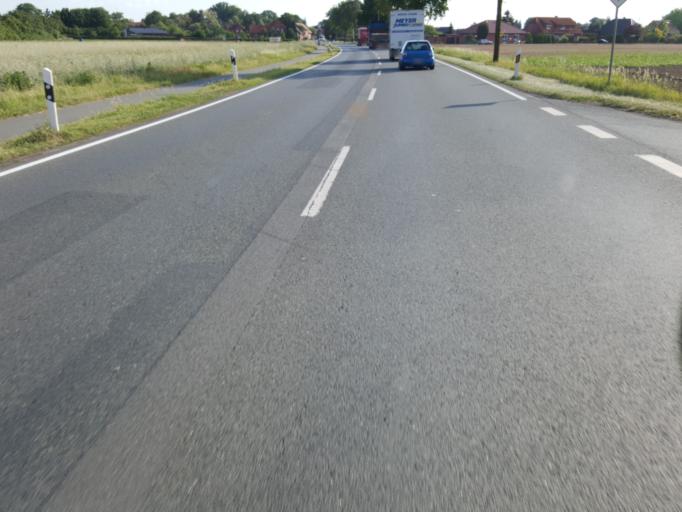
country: DE
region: Lower Saxony
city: Estorf
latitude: 52.5932
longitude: 9.1484
